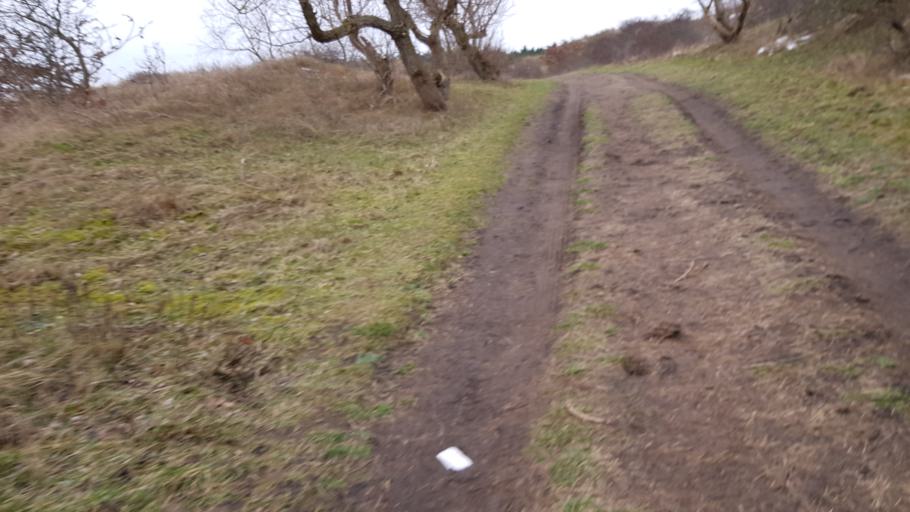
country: NL
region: North Holland
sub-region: Gemeente Bergen
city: Egmond aan Zee
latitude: 52.6004
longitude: 4.6287
